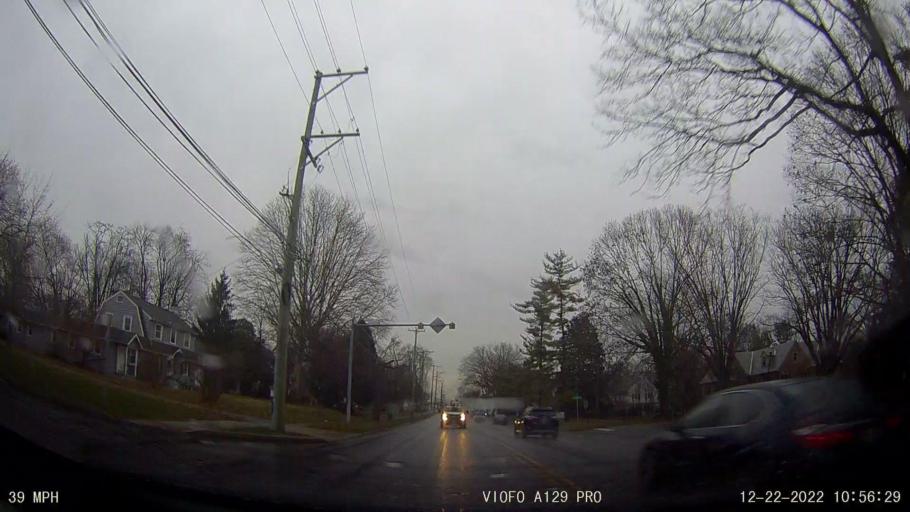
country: US
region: Pennsylvania
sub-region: Montgomery County
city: West Norriton
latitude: 40.1261
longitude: -75.3669
